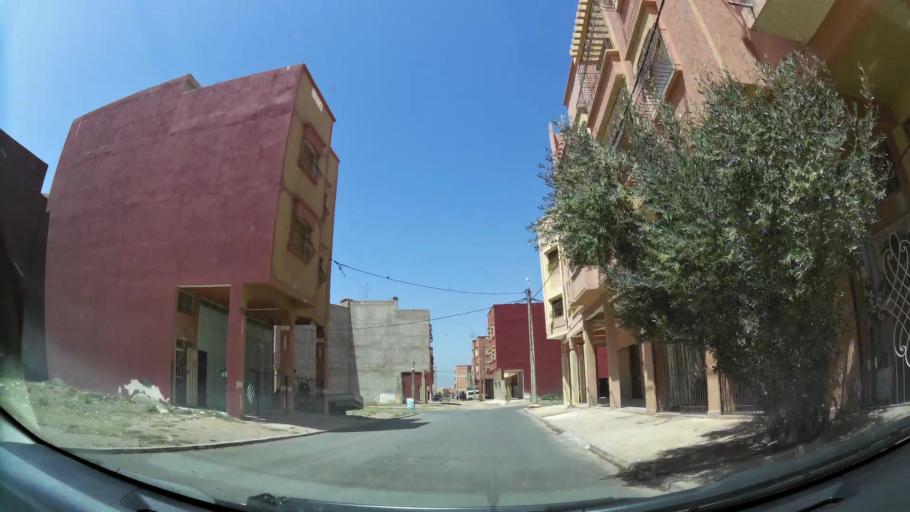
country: MA
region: Souss-Massa-Draa
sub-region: Inezgane-Ait Mellou
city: Inezgane
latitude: 30.3459
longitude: -9.4830
